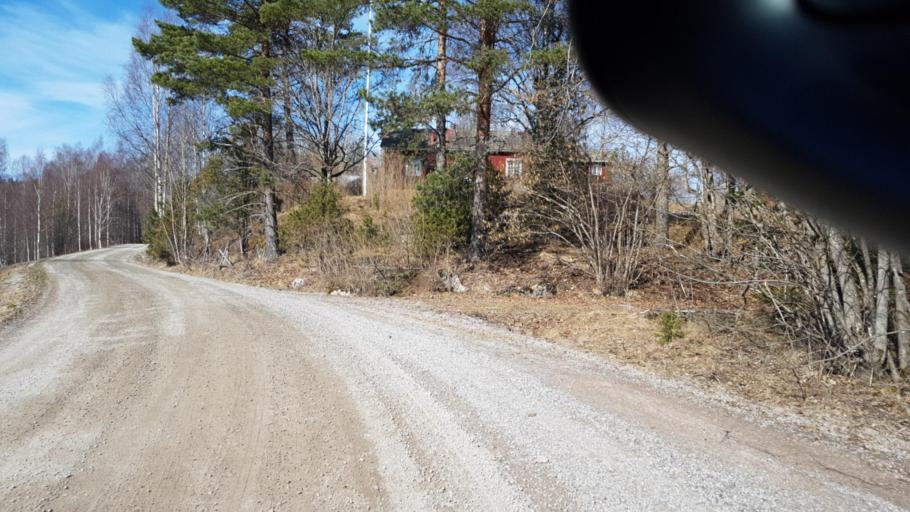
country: SE
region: Vaermland
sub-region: Sunne Kommun
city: Sunne
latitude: 59.7030
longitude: 12.8869
